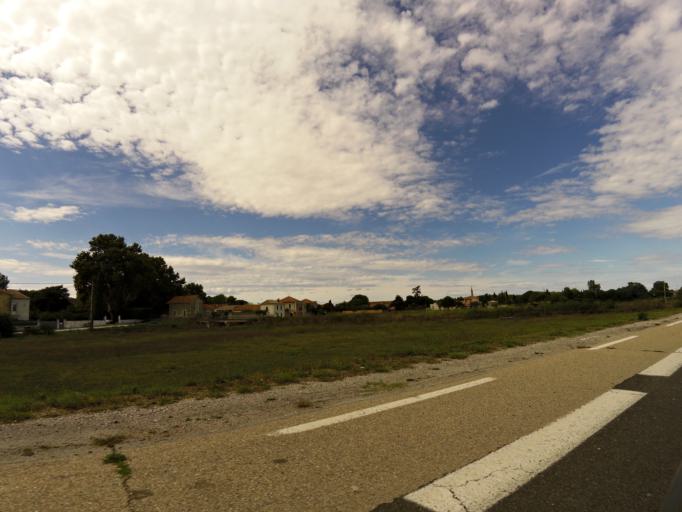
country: FR
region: Languedoc-Roussillon
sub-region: Departement du Gard
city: Aimargues
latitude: 43.6785
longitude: 4.2108
